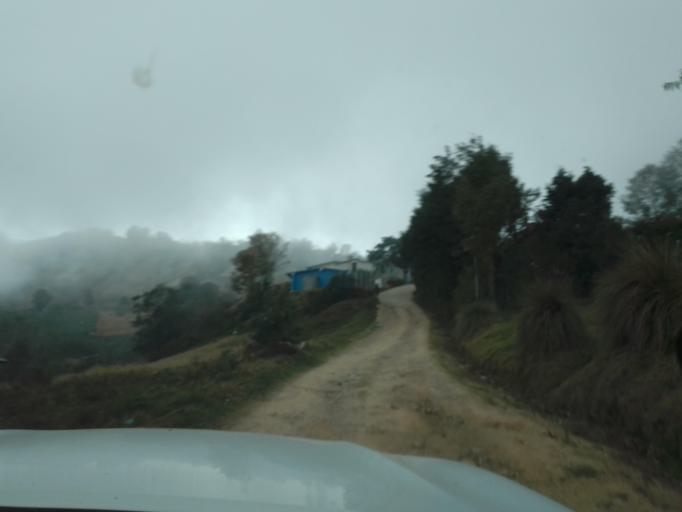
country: MX
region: Chiapas
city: Motozintla de Mendoza
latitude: 15.2199
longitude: -92.2198
